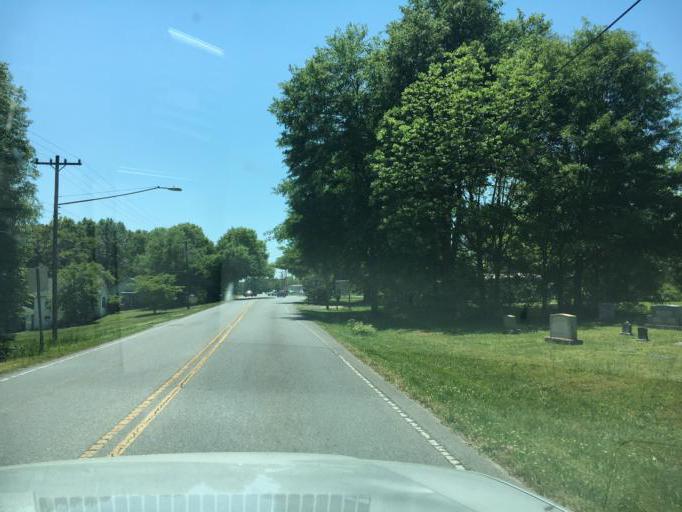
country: US
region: North Carolina
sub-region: Cleveland County
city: Shelby
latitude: 35.2588
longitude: -81.5632
